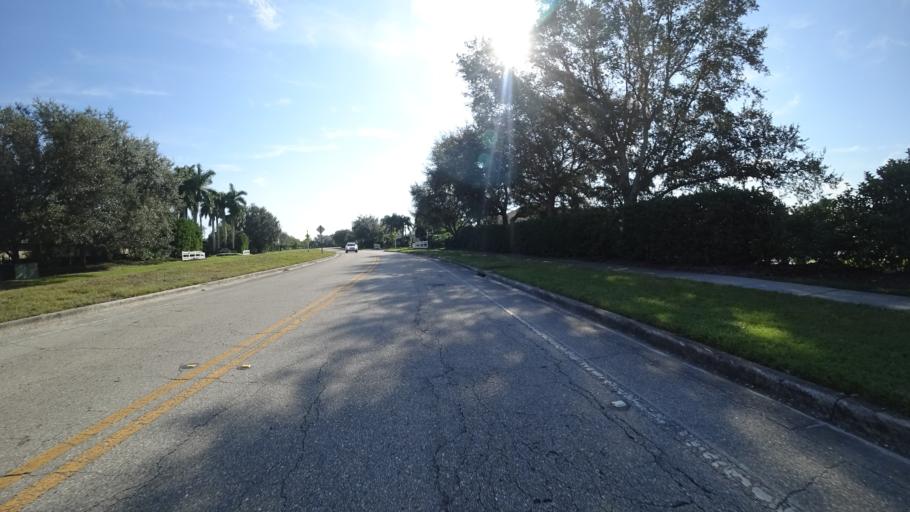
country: US
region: Florida
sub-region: Sarasota County
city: Desoto Lakes
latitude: 27.4178
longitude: -82.4795
